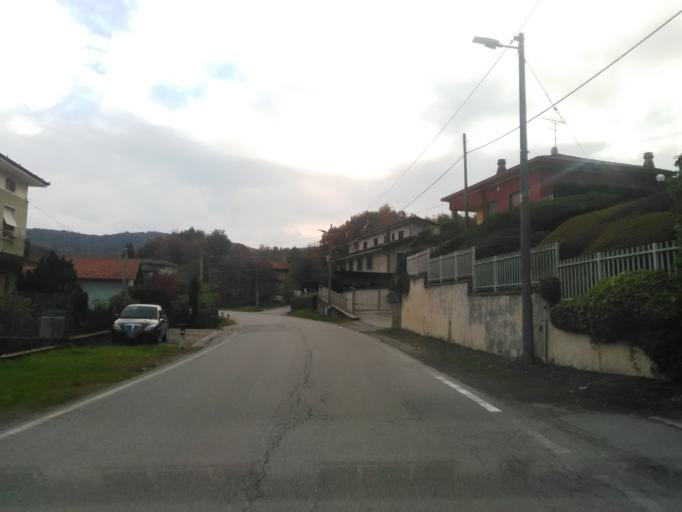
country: IT
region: Piedmont
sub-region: Provincia di Novara
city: Pogno
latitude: 45.7551
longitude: 8.3804
